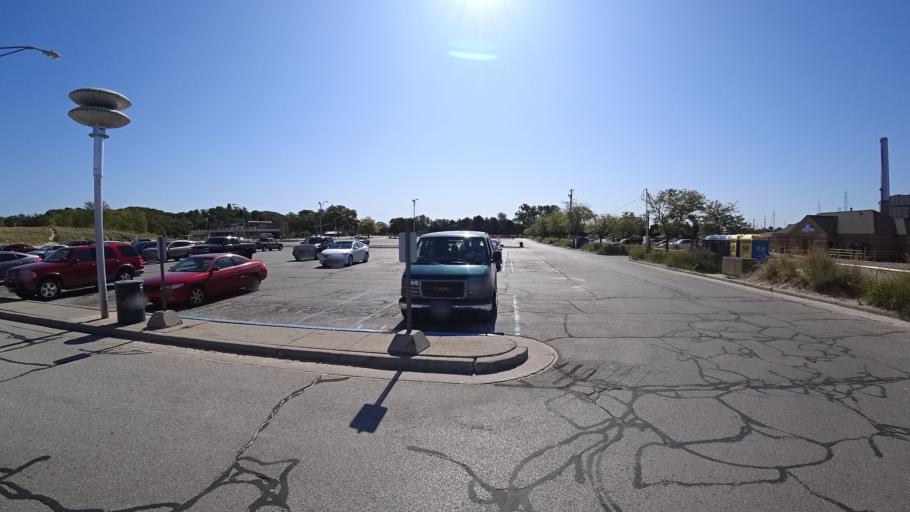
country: US
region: Indiana
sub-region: LaPorte County
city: Michigan City
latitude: 41.7279
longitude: -86.9051
